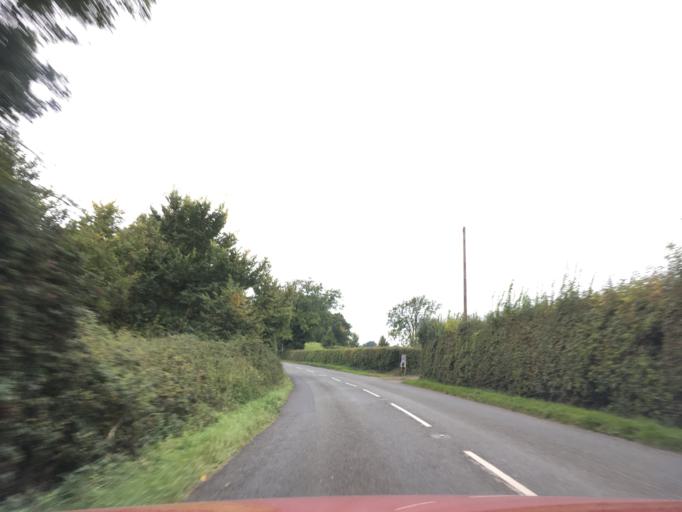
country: GB
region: England
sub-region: South Gloucestershire
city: Almondsbury
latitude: 51.5944
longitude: -2.5898
